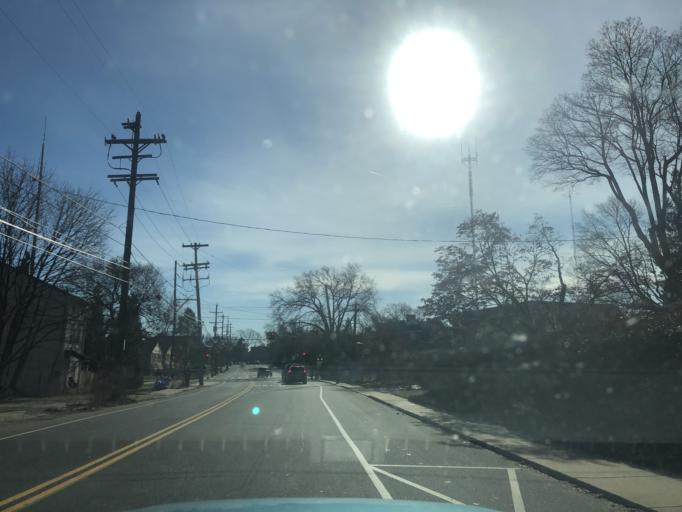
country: US
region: Pennsylvania
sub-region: Montgomery County
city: Bala-Cynwyd
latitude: 40.0496
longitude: -75.2358
